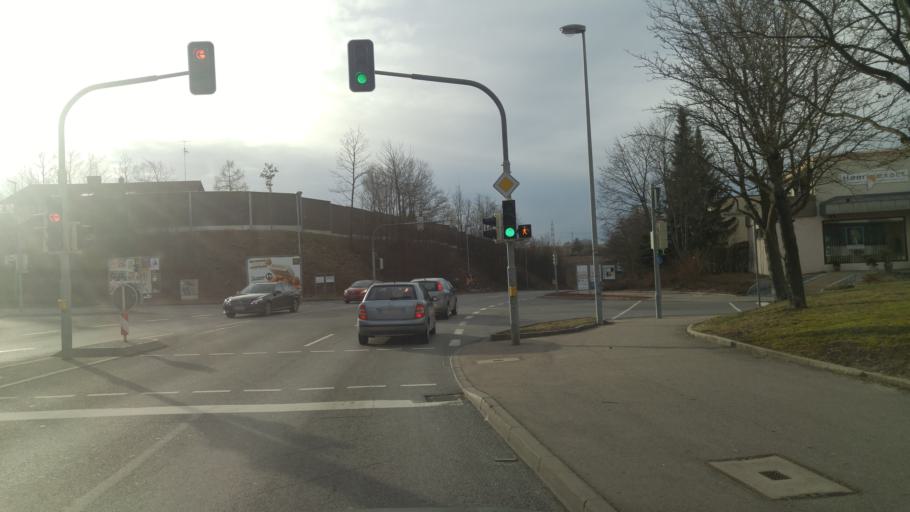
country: DE
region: Baden-Wuerttemberg
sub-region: Regierungsbezirk Stuttgart
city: Leonberg
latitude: 48.7935
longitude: 8.9986
